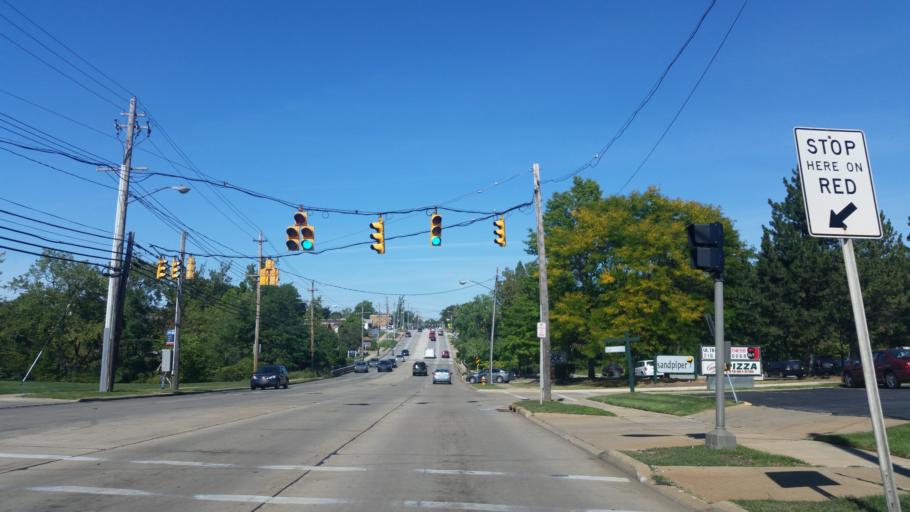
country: US
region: Ohio
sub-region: Cuyahoga County
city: Brooklyn Heights
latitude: 41.4101
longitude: -81.6925
